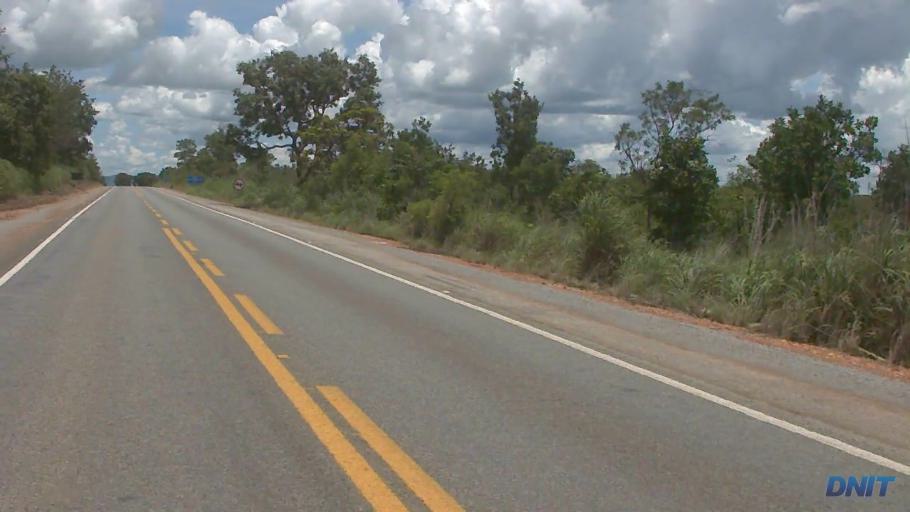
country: BR
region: Goias
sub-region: Barro Alto
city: Barro Alto
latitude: -14.7834
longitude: -49.0542
